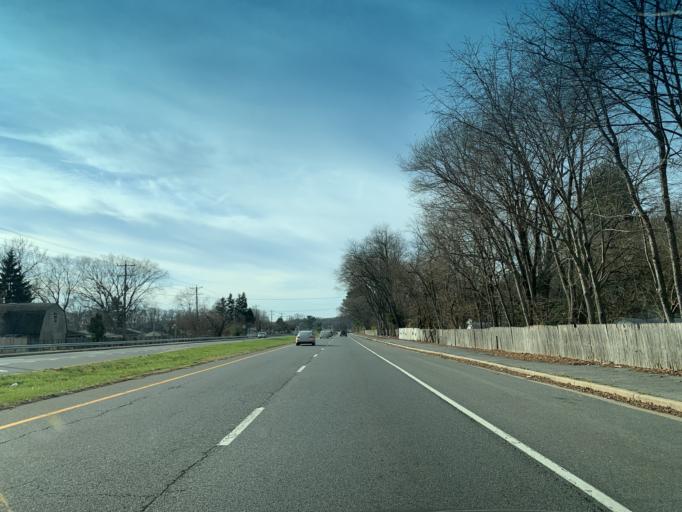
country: US
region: Delaware
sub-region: New Castle County
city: Brookside
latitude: 39.6622
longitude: -75.7308
